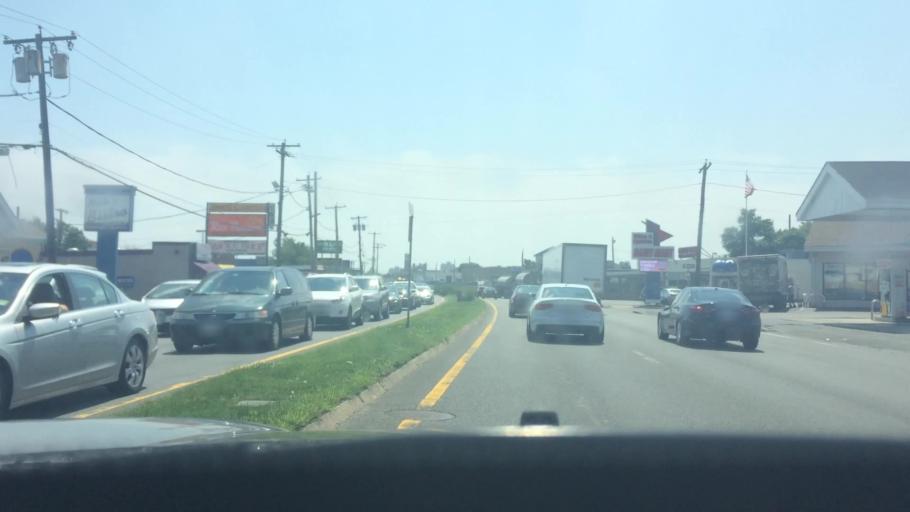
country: US
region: Massachusetts
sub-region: Suffolk County
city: Revere
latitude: 42.4242
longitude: -71.0104
